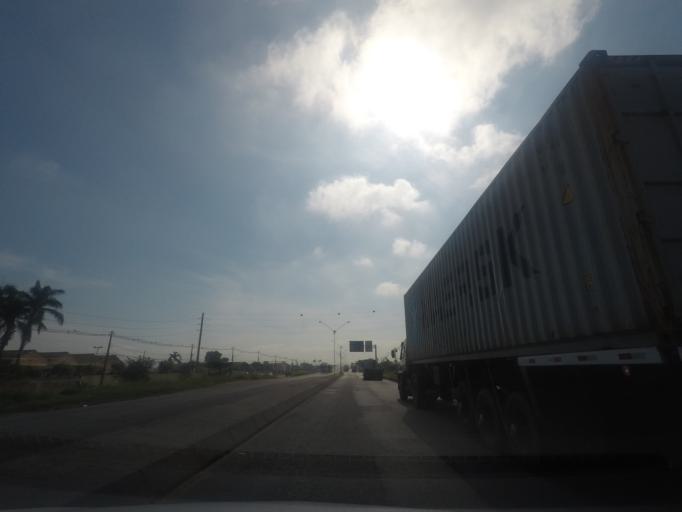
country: BR
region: Parana
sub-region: Paranagua
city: Paranagua
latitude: -25.5286
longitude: -48.5281
